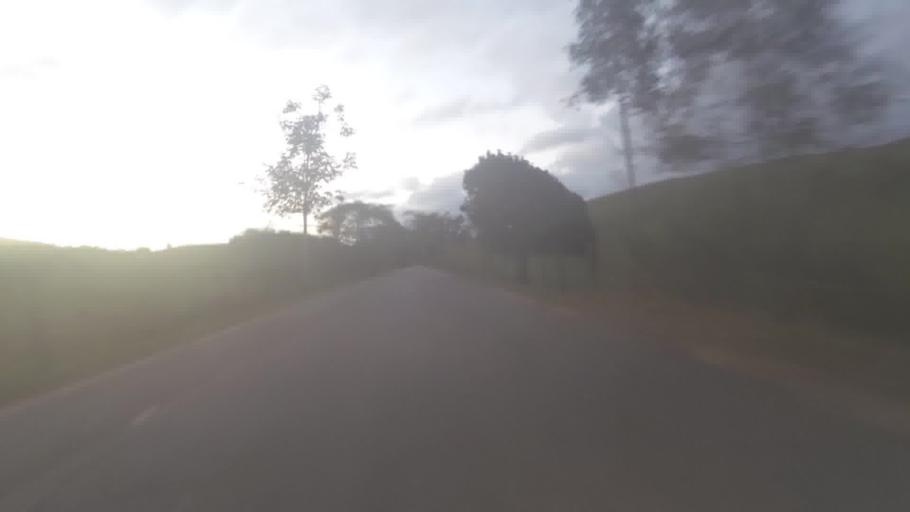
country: BR
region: Espirito Santo
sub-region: Itapemirim
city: Itapemirim
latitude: -20.9500
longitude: -40.8795
